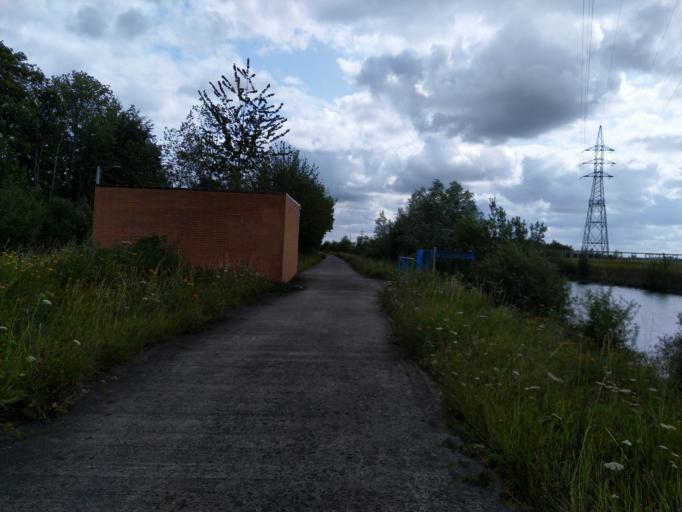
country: BE
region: Wallonia
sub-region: Province du Hainaut
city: Quaregnon
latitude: 50.4754
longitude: 3.8559
